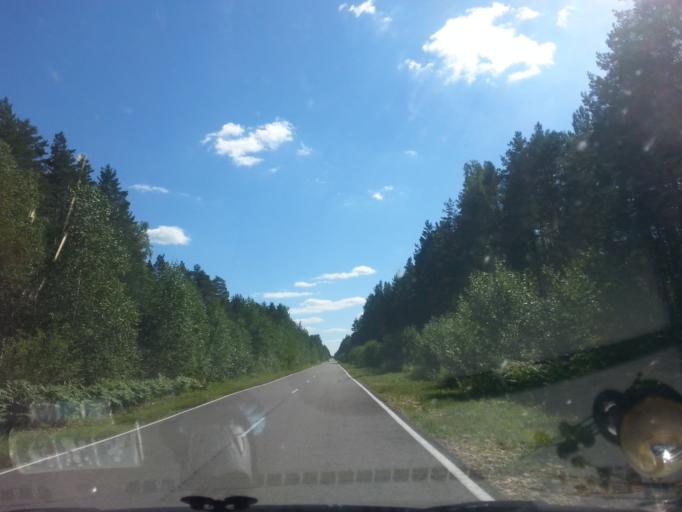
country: RU
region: Vladimir
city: Galitsy
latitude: 56.0877
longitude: 42.8687
